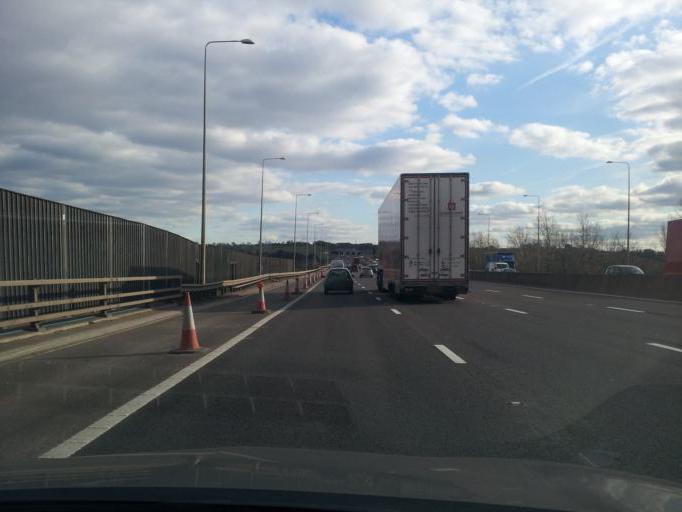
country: GB
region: England
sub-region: Derbyshire
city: Pinxton
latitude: 53.0925
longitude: -1.3076
